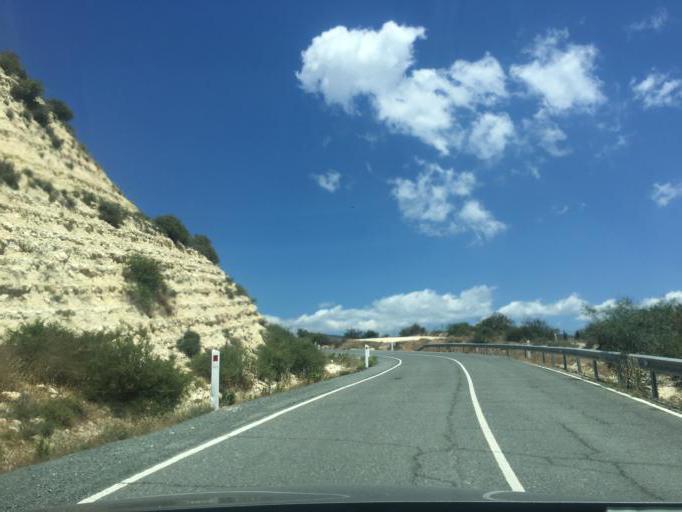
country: CY
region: Limassol
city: Mouttagiaka
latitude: 34.7614
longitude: 33.0620
